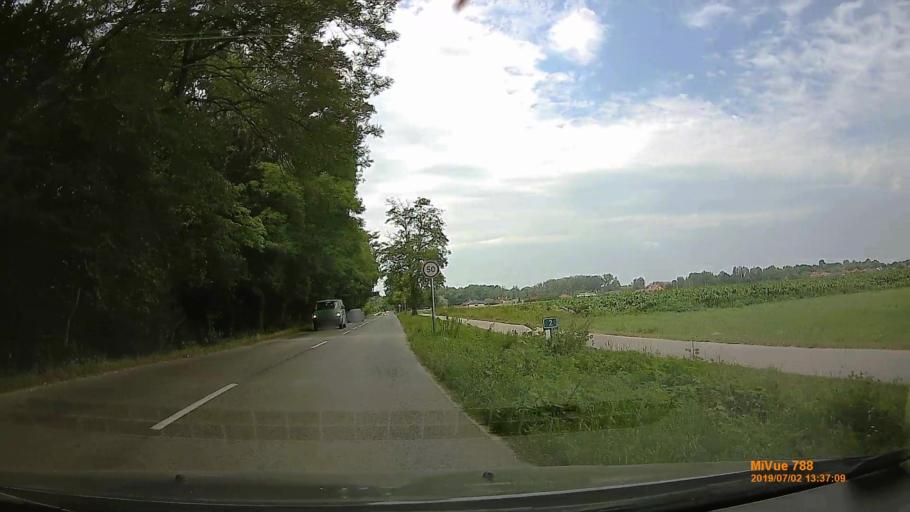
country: HU
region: Gyor-Moson-Sopron
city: Mosonmagyarovar
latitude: 47.8544
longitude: 17.3005
